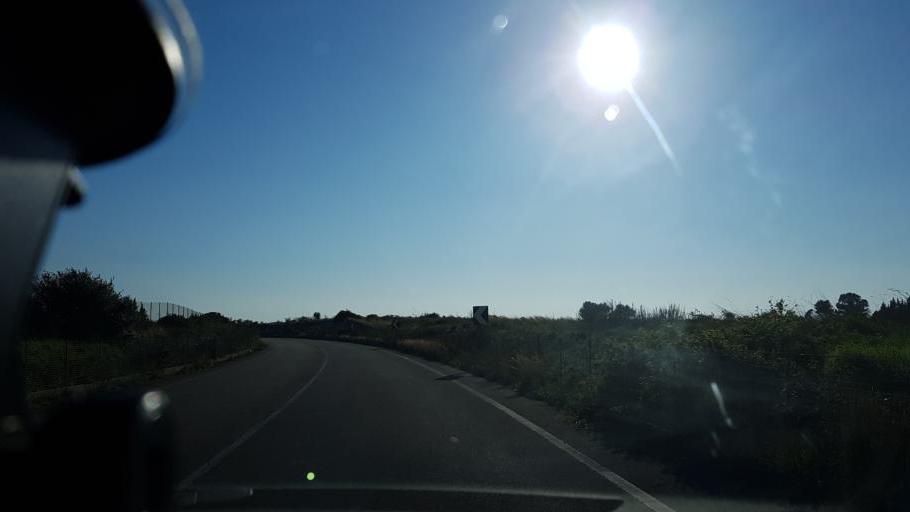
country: IT
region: Apulia
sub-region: Provincia di Lecce
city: Merine
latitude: 40.4064
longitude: 18.2519
